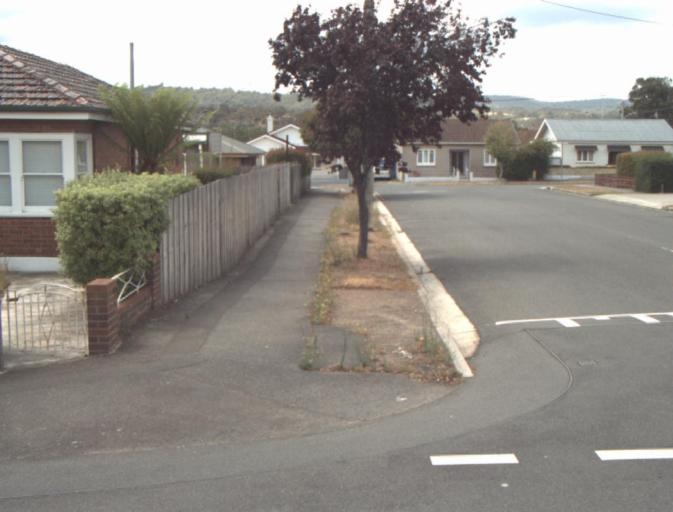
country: AU
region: Tasmania
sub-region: Launceston
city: Newnham
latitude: -41.4029
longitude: 147.1345
